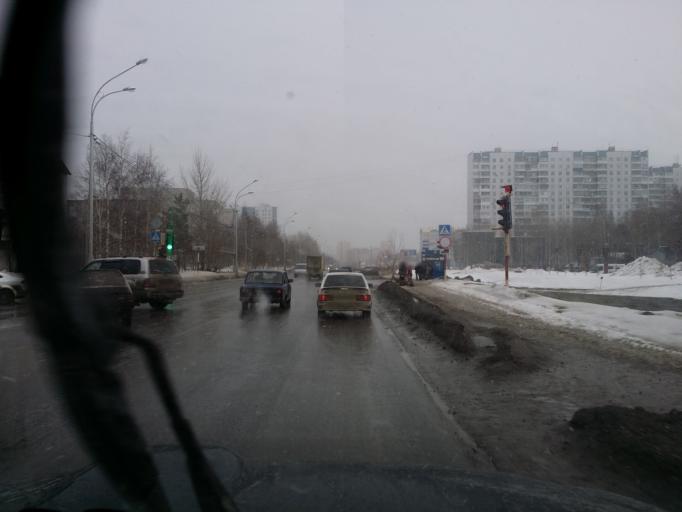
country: RU
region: Khanty-Mansiyskiy Avtonomnyy Okrug
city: Nizhnevartovsk
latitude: 60.9307
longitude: 76.5491
